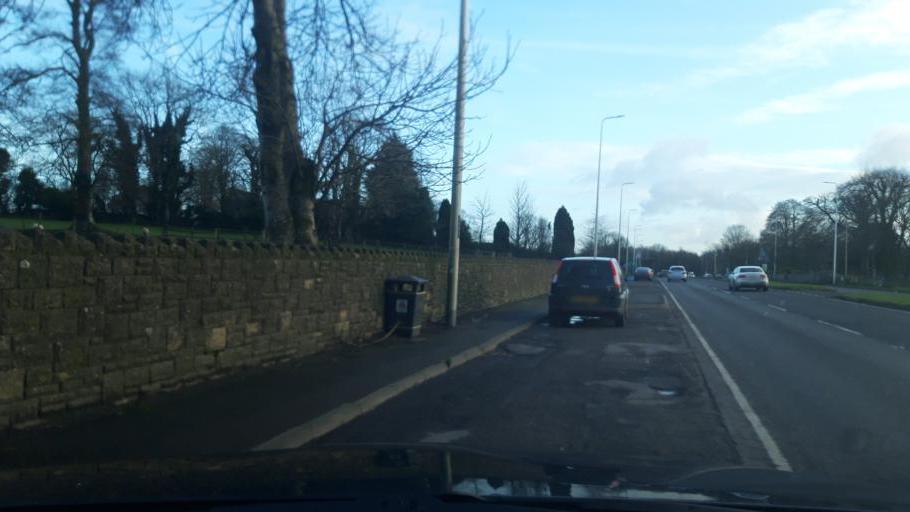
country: GB
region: Northern Ireland
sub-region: Dungannon District
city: Dungannon
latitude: 54.4856
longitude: -6.7421
